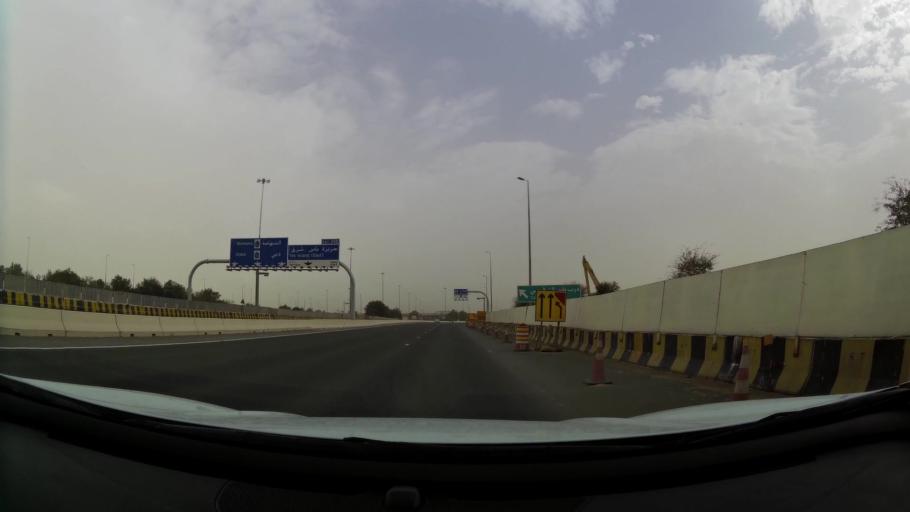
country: AE
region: Abu Dhabi
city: Abu Dhabi
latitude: 24.4778
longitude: 54.6389
